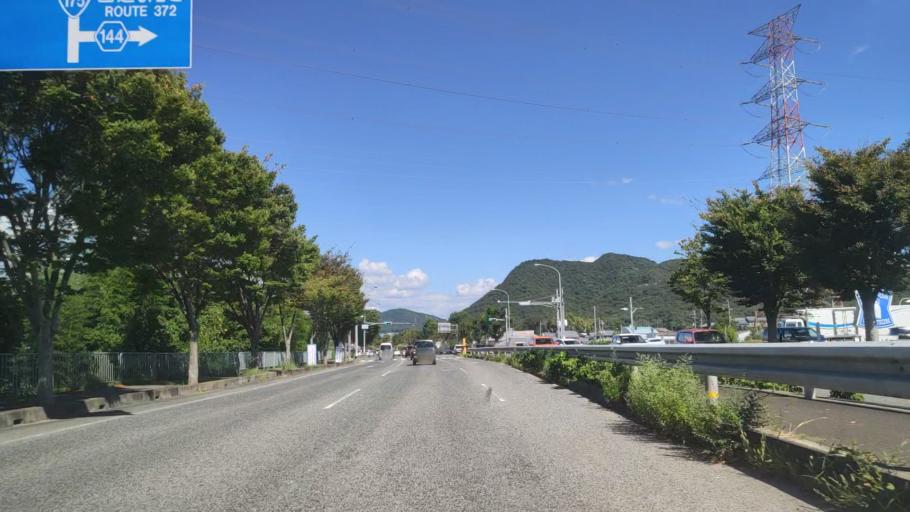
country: JP
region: Hyogo
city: Nishiwaki
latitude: 34.9578
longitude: 134.9735
